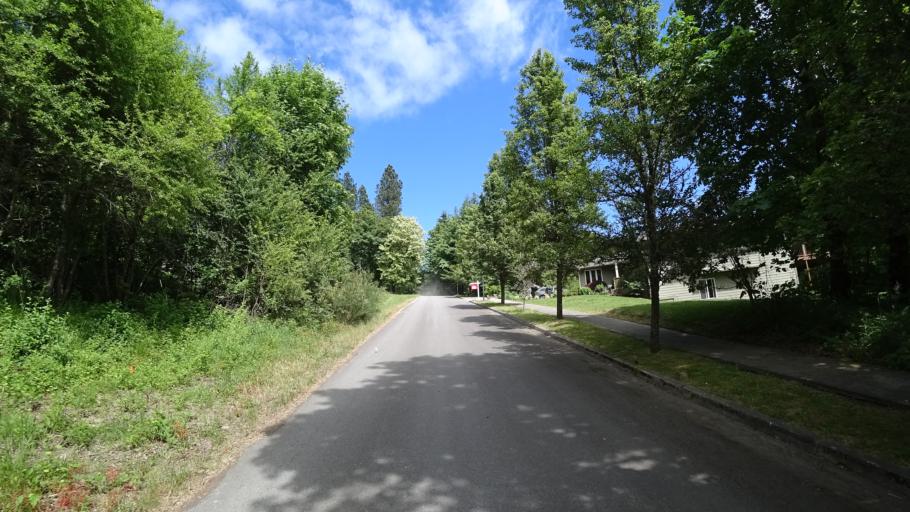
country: US
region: Oregon
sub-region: Washington County
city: Bethany
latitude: 45.5973
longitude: -122.8307
